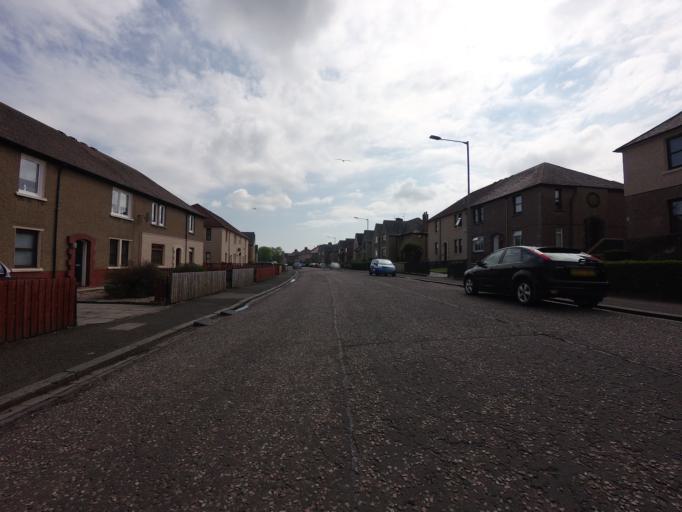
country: GB
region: Scotland
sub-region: Falkirk
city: Falkirk
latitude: 56.0016
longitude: -3.7680
